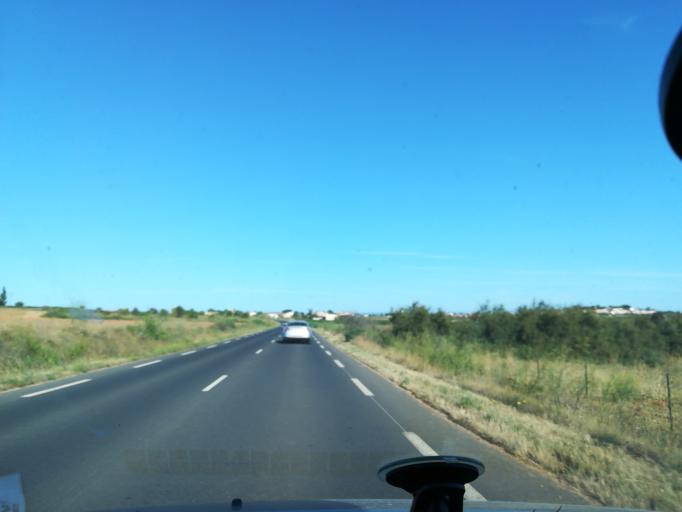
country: FR
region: Languedoc-Roussillon
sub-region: Departement de l'Herault
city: Portiragnes
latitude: 43.2956
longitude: 3.3534
